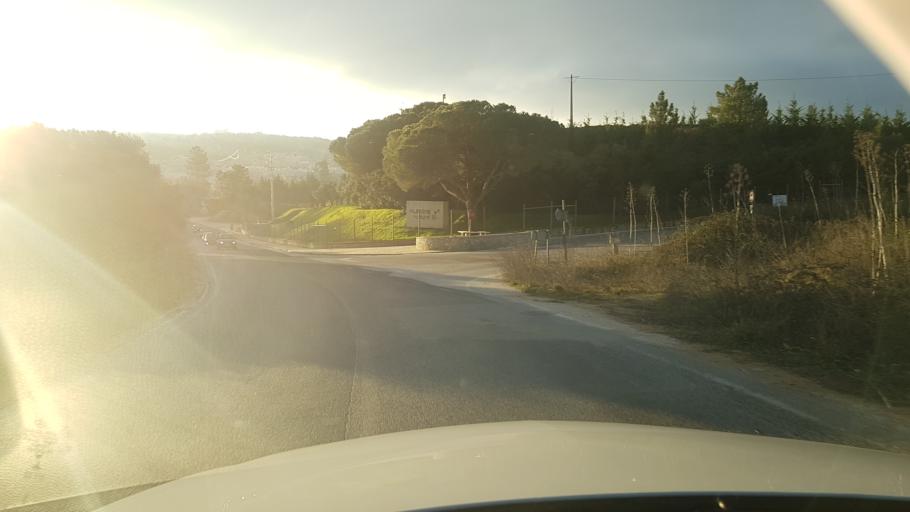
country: PT
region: Santarem
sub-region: Ourem
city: Fatima
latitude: 39.5758
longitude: -8.6145
